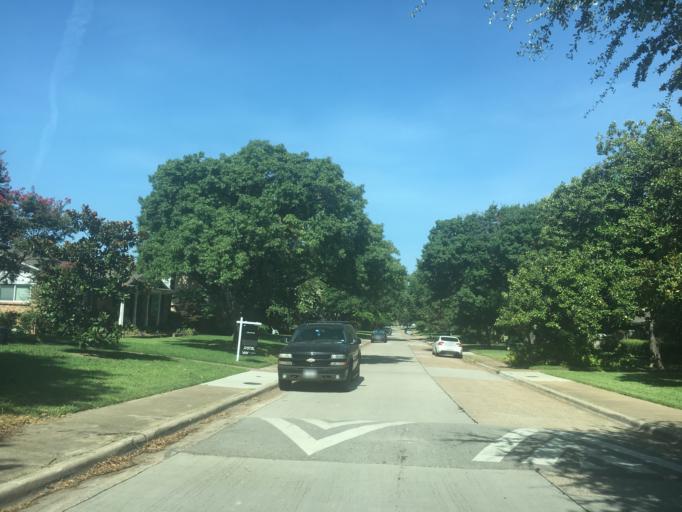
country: US
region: Texas
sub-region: Dallas County
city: Richardson
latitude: 32.8764
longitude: -96.7189
